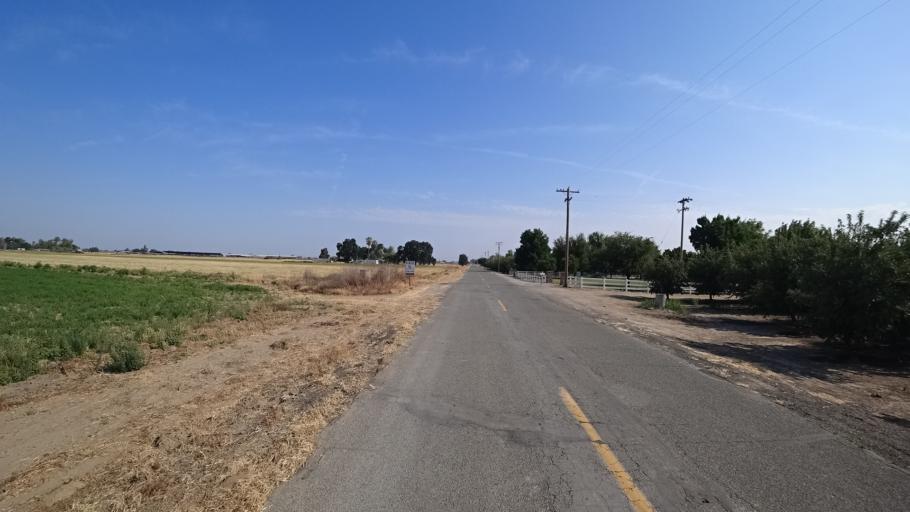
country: US
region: California
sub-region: Fresno County
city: Riverdale
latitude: 36.3692
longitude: -119.8341
